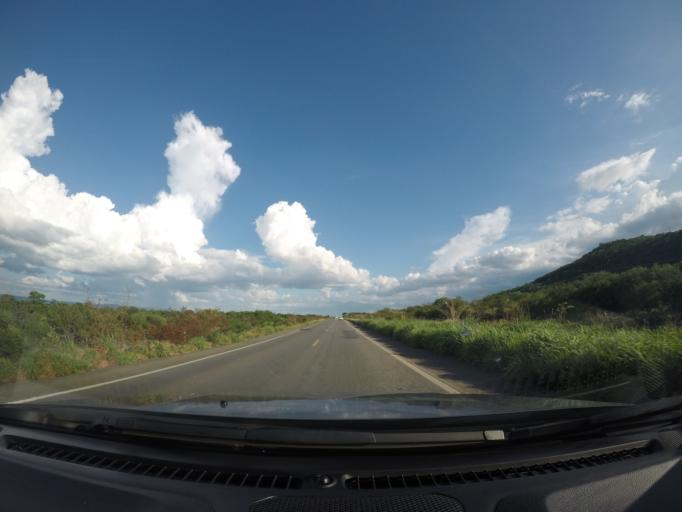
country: BR
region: Bahia
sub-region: Oliveira Dos Brejinhos
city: Oliveira dos Brejinhos
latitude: -12.0760
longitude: -42.9483
